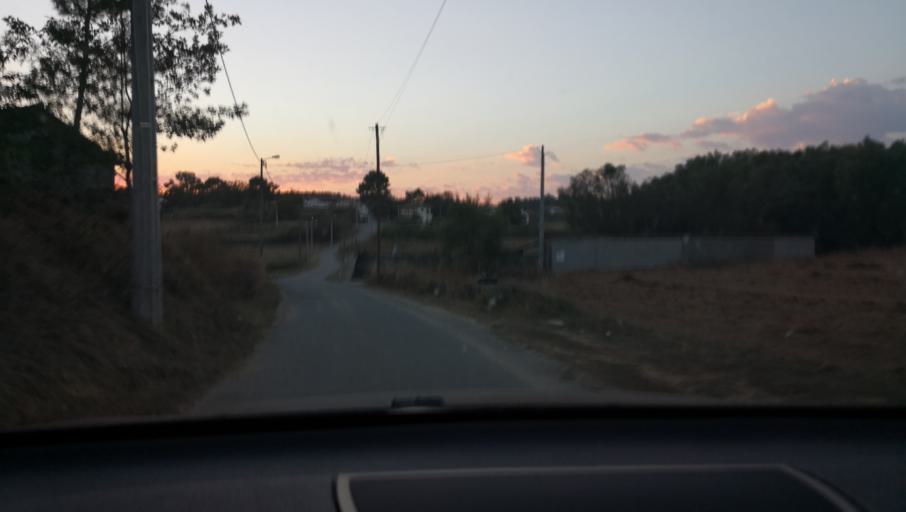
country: PT
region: Vila Real
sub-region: Sabrosa
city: Vilela
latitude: 41.2479
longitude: -7.6314
